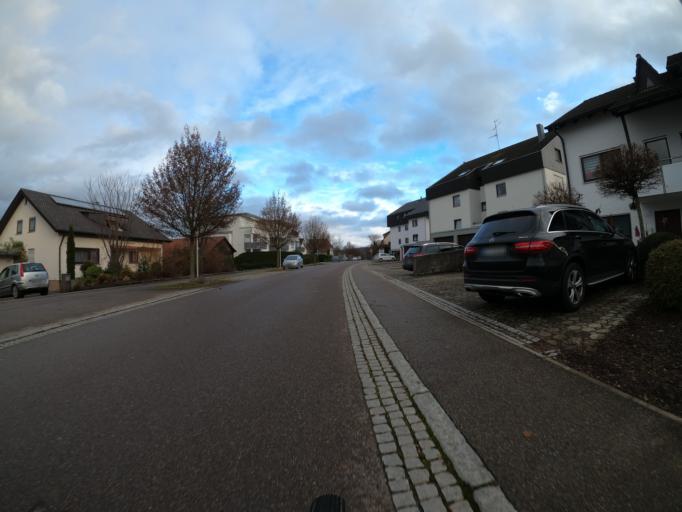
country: DE
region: Baden-Wuerttemberg
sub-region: Regierungsbezirk Stuttgart
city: Eislingen
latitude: 48.6910
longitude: 9.7103
